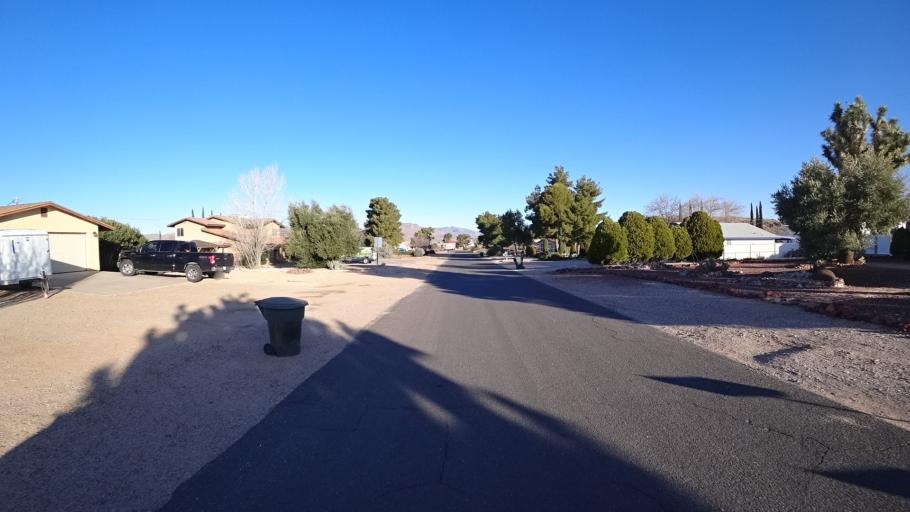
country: US
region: Arizona
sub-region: Mohave County
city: Kingman
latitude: 35.2053
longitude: -114.0087
